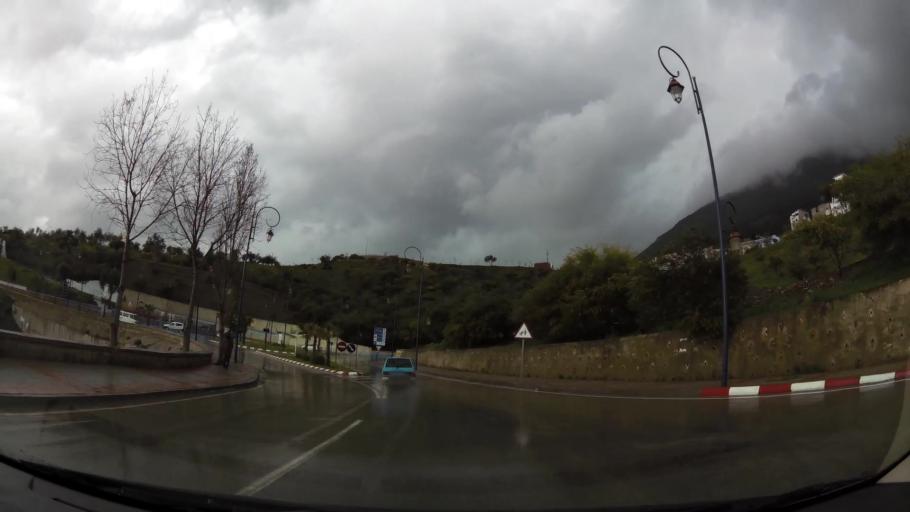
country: MA
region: Tanger-Tetouan
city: Chefchaouene
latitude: 35.1726
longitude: -5.2730
